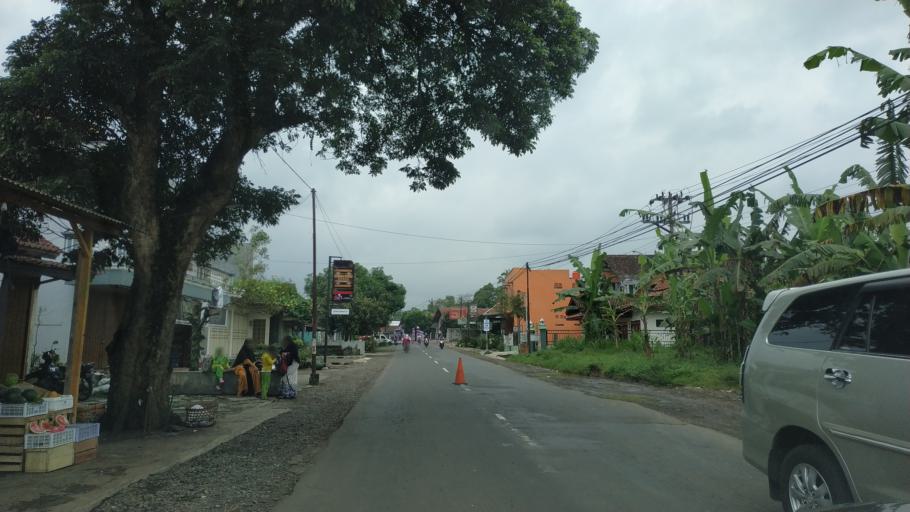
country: ID
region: Central Java
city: Weleri
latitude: -7.0808
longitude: 110.0430
